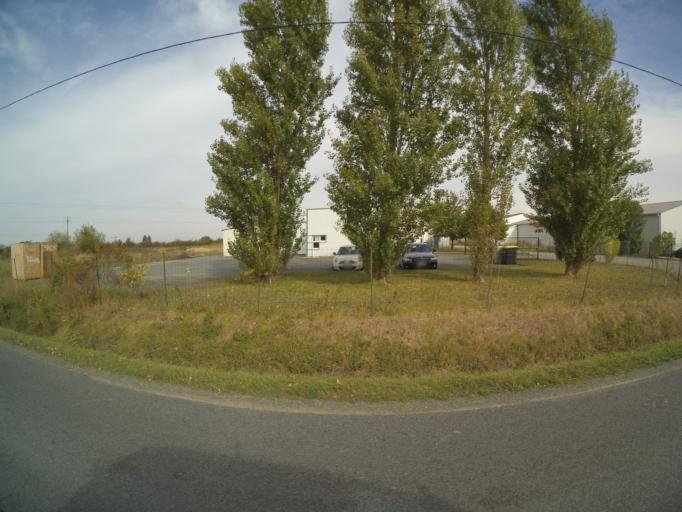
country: FR
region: Pays de la Loire
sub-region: Departement de Maine-et-Loire
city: Martigne-Briand
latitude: 47.2068
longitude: -0.4645
